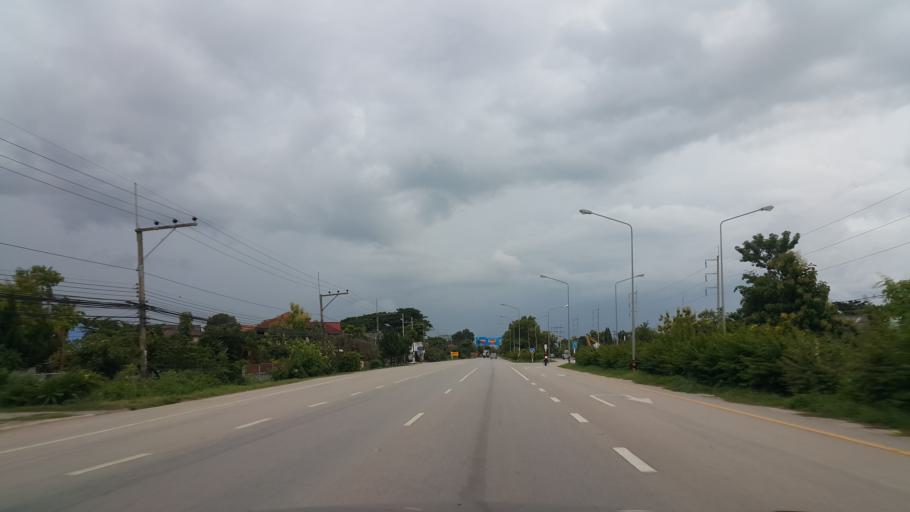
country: TH
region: Phayao
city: Phayao
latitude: 19.1222
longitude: 99.9078
